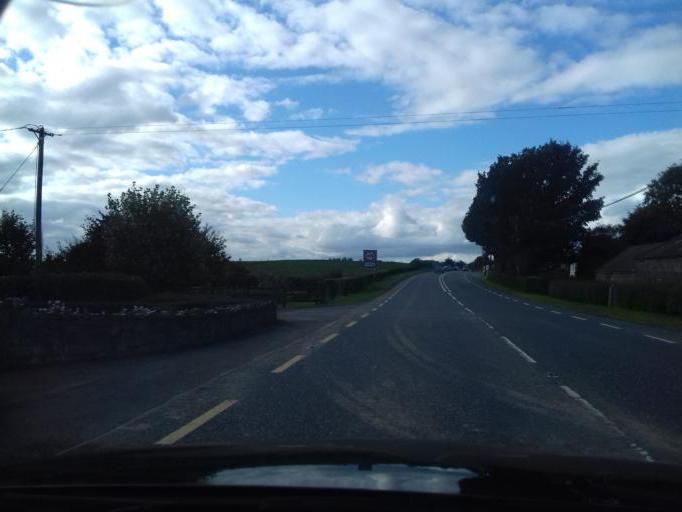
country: IE
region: Leinster
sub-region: Uibh Fhaili
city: Tullamore
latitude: 53.3109
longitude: -7.5016
